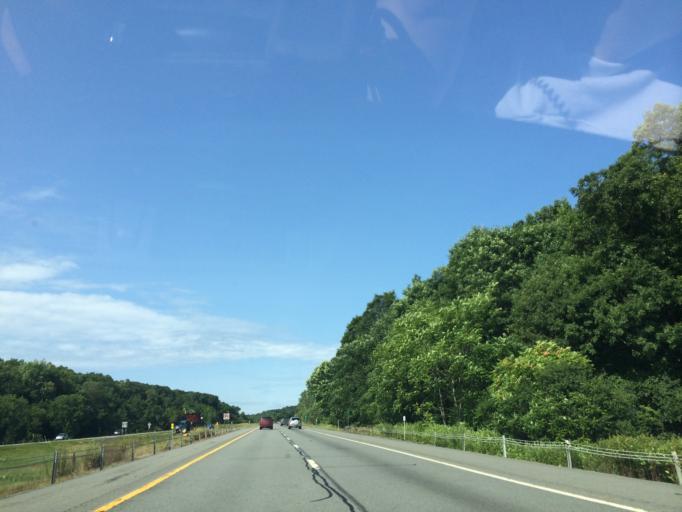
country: US
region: New York
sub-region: Orange County
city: Otisville
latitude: 41.4003
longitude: -74.5208
